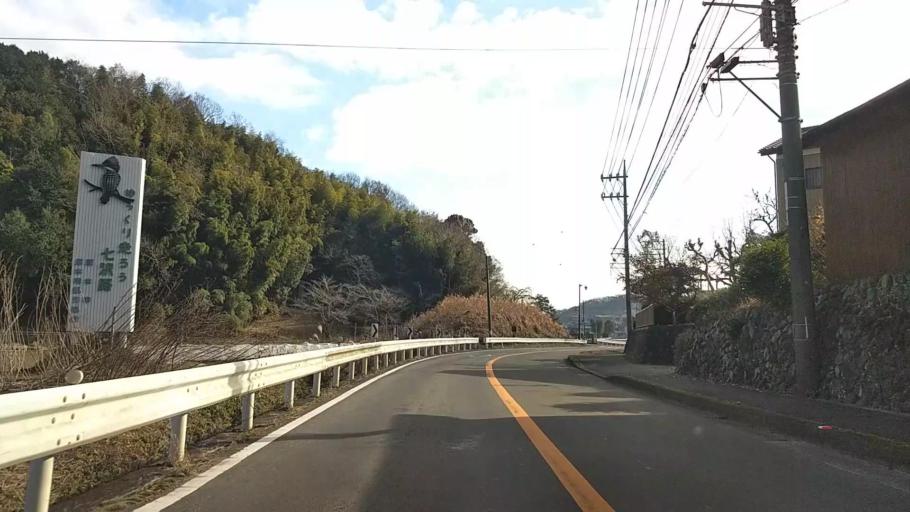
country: JP
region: Kanagawa
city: Isehara
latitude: 35.4377
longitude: 139.3035
